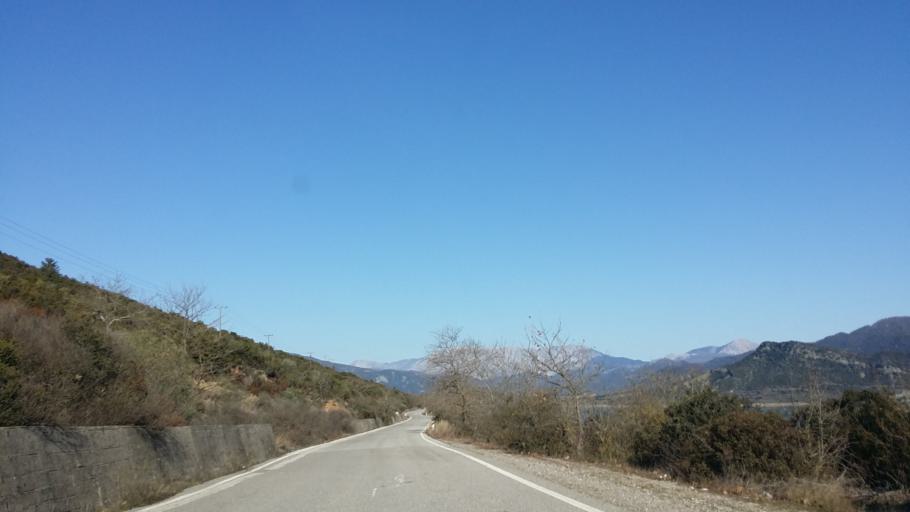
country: GR
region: West Greece
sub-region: Nomos Aitolias kai Akarnanias
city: Lepenou
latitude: 38.8132
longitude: 21.3347
